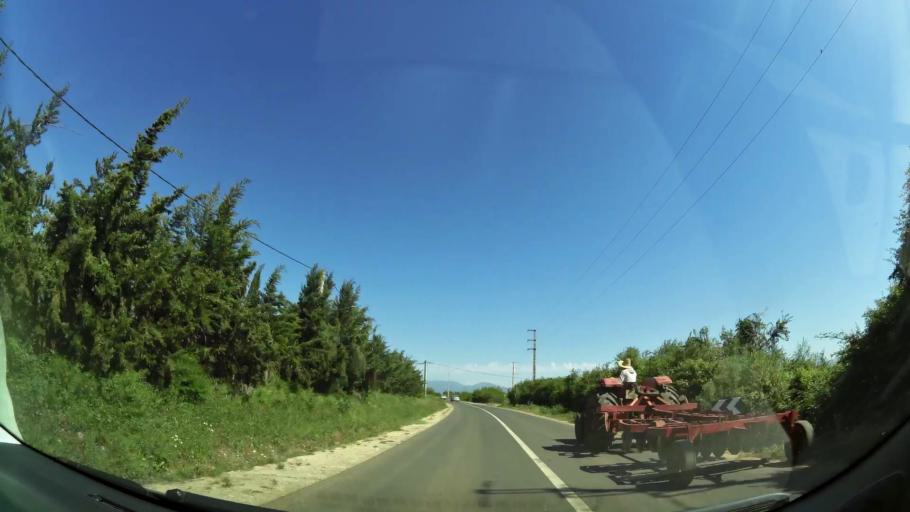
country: MA
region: Oriental
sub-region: Berkane-Taourirt
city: Madagh
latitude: 35.0172
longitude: -2.4064
